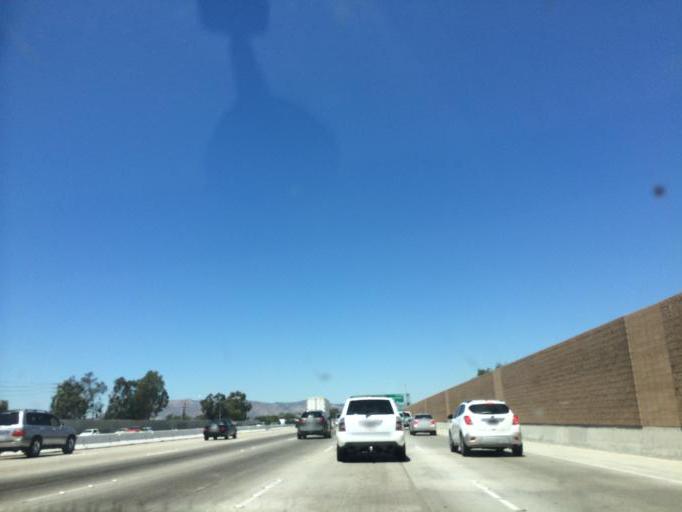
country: US
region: California
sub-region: Los Angeles County
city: San Fernando
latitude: 34.2520
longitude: -118.4298
